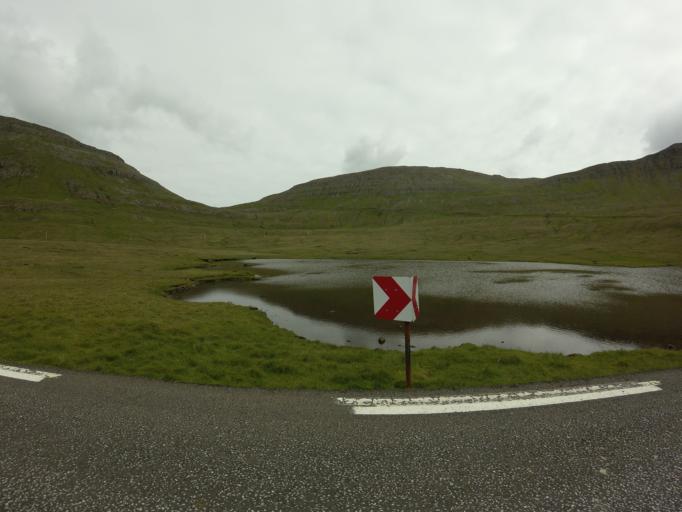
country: FO
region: Suduroy
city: Tvoroyri
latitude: 61.5184
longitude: -6.8486
